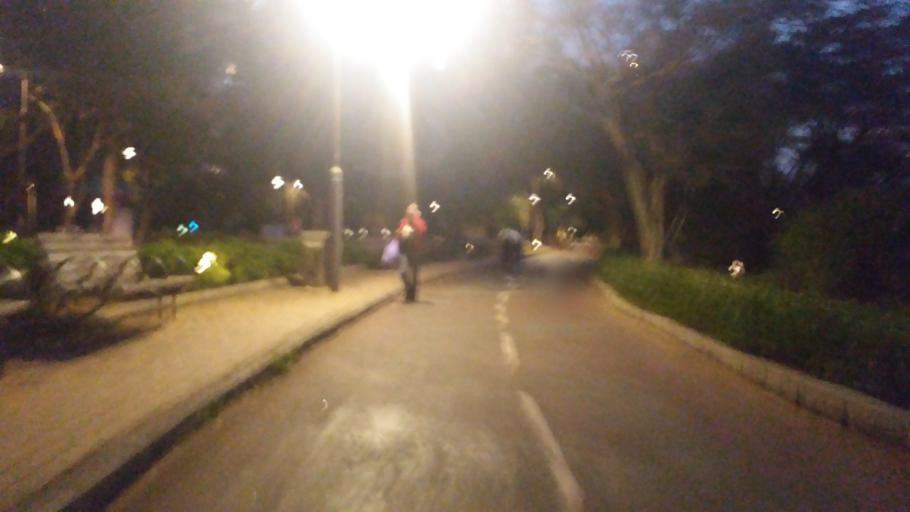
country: HK
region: Yuen Long
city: Yuen Long Kau Hui
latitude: 22.4527
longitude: 113.9982
